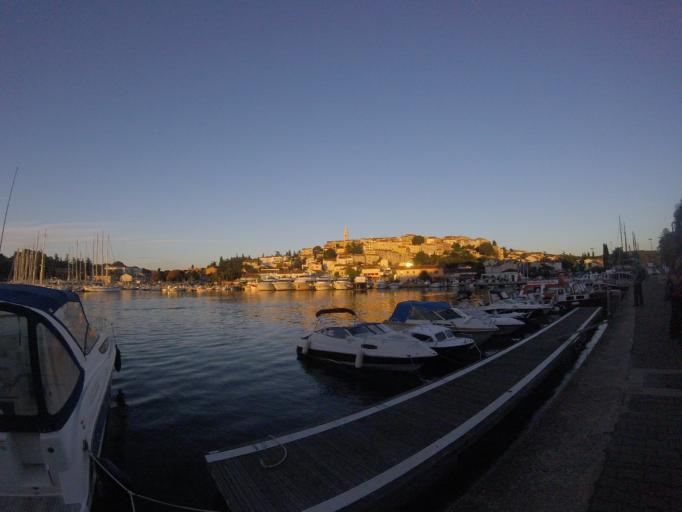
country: HR
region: Istarska
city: Vrsar
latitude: 45.1487
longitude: 13.6017
